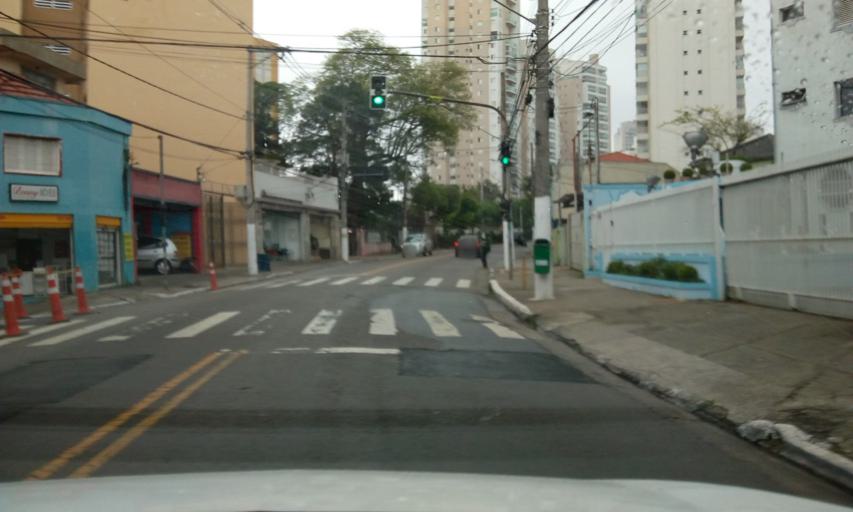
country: BR
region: Sao Paulo
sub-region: Sao Paulo
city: Sao Paulo
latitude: -23.5863
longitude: -46.6281
